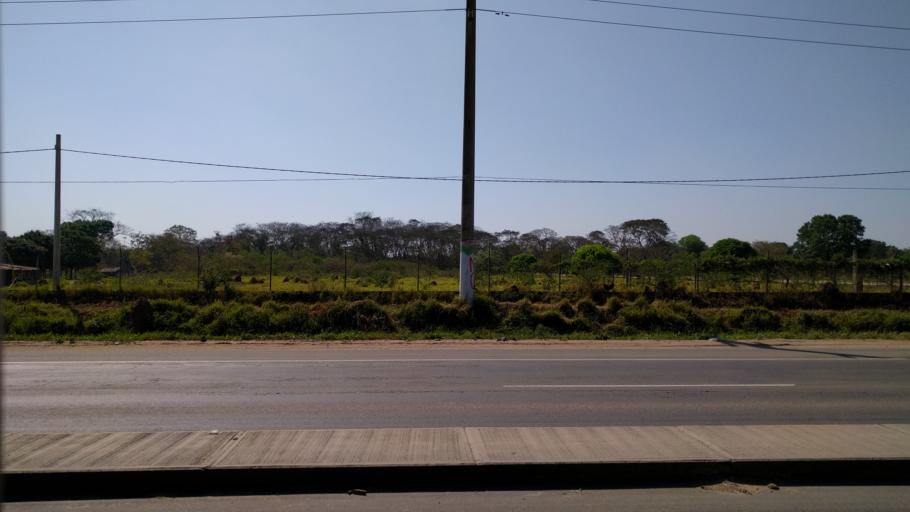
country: BO
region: Santa Cruz
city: Cotoca
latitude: -17.7669
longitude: -63.0506
